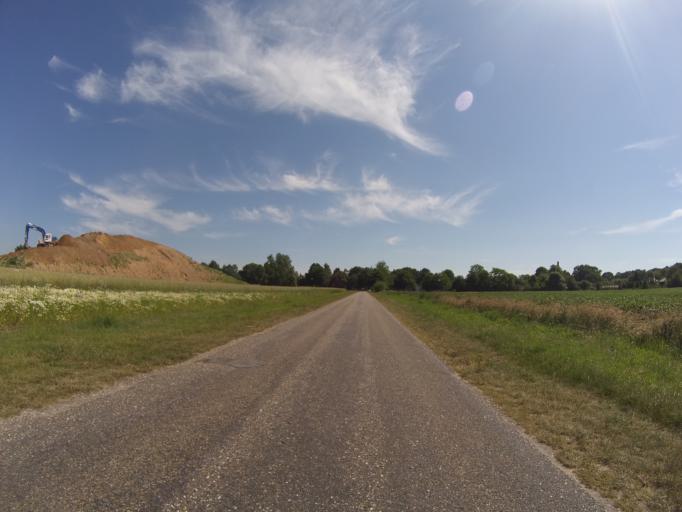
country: NL
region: Drenthe
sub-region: Gemeente Emmen
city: Emmen
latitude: 52.7773
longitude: 6.8825
